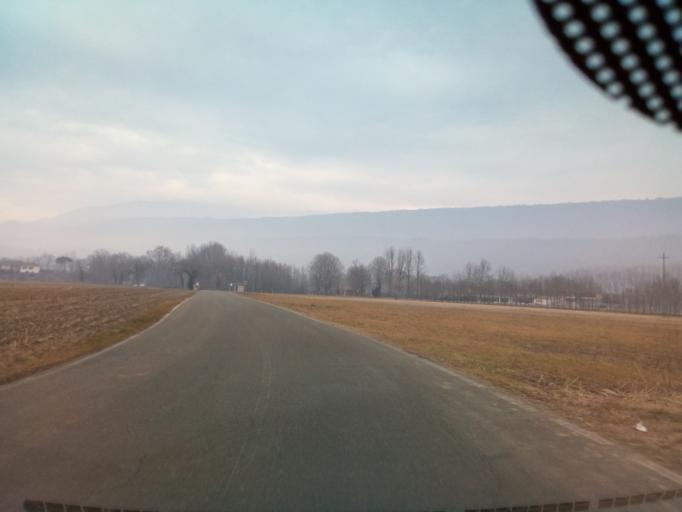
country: IT
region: Piedmont
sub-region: Provincia di Torino
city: Burolo
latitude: 45.4771
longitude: 7.9205
